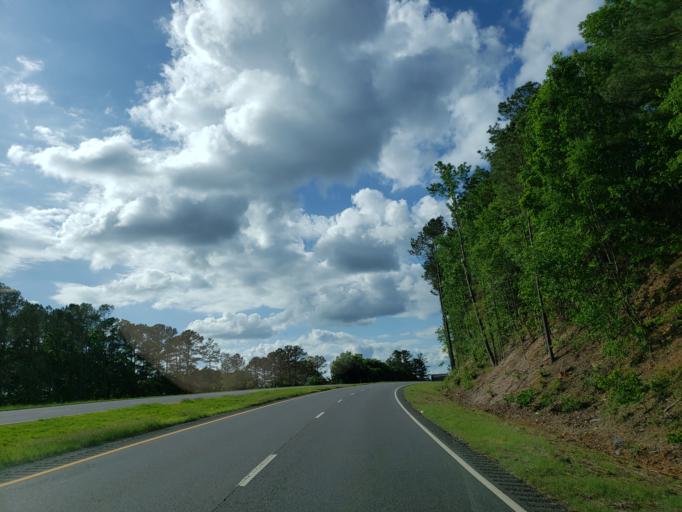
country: US
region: Georgia
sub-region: Bartow County
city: Cartersville
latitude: 34.2225
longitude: -84.8524
